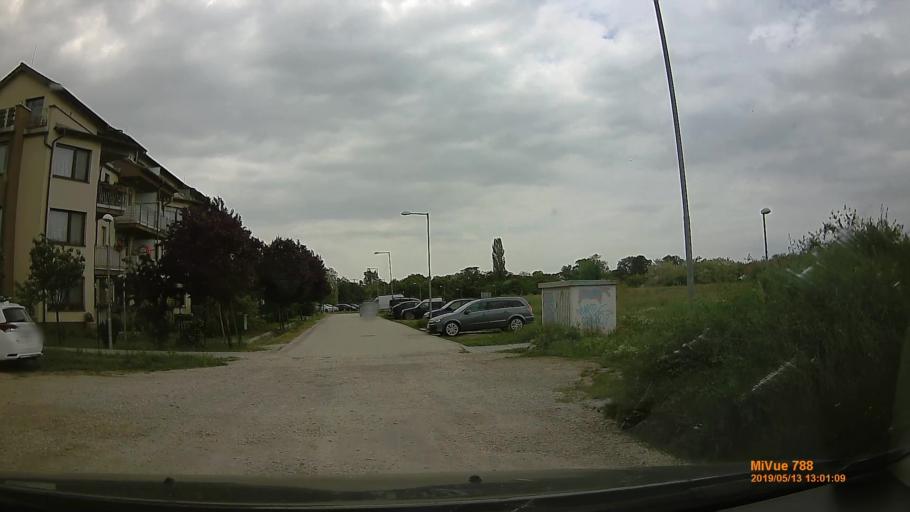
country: HU
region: Pest
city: Halasztelek
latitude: 47.4011
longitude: 18.9979
